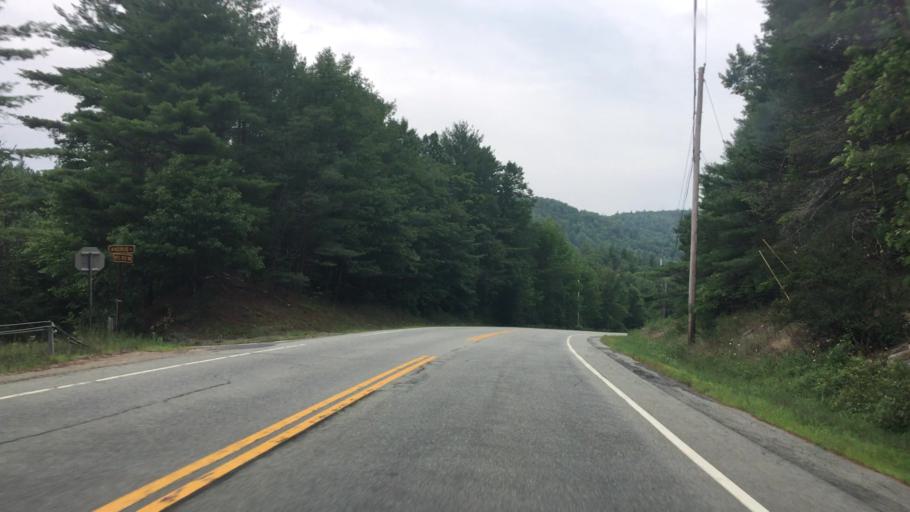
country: US
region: New York
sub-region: Essex County
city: Lake Placid
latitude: 44.3127
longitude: -73.7856
